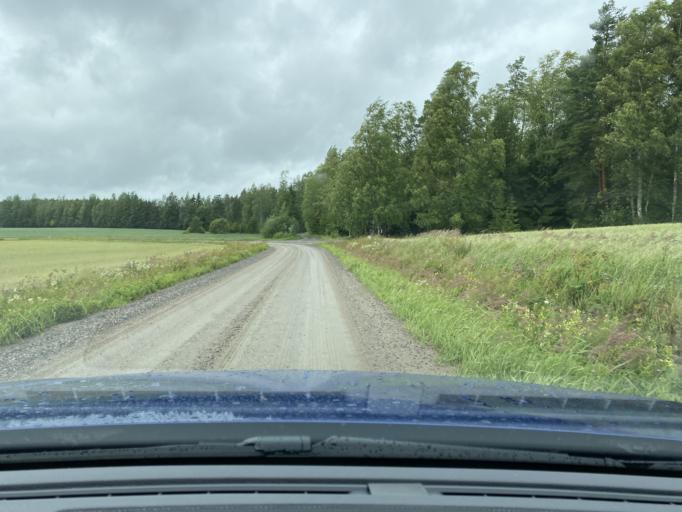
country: FI
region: Pirkanmaa
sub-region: Lounais-Pirkanmaa
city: Punkalaidun
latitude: 61.1504
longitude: 23.2283
